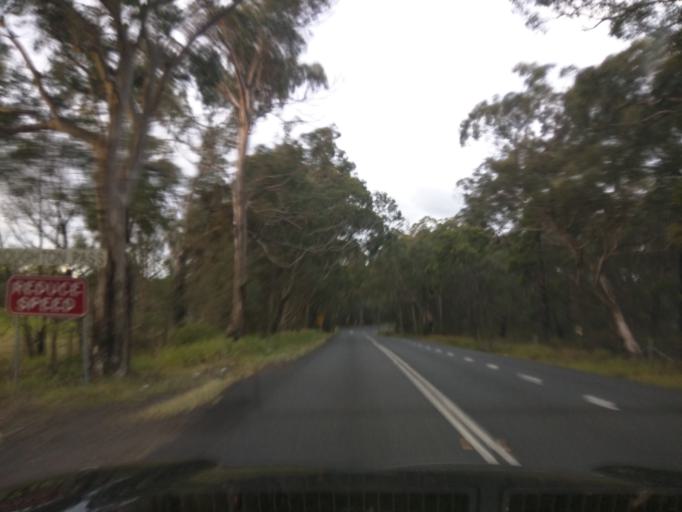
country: AU
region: New South Wales
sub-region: Wollondilly
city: Douglas Park
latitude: -34.2309
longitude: 150.7383
